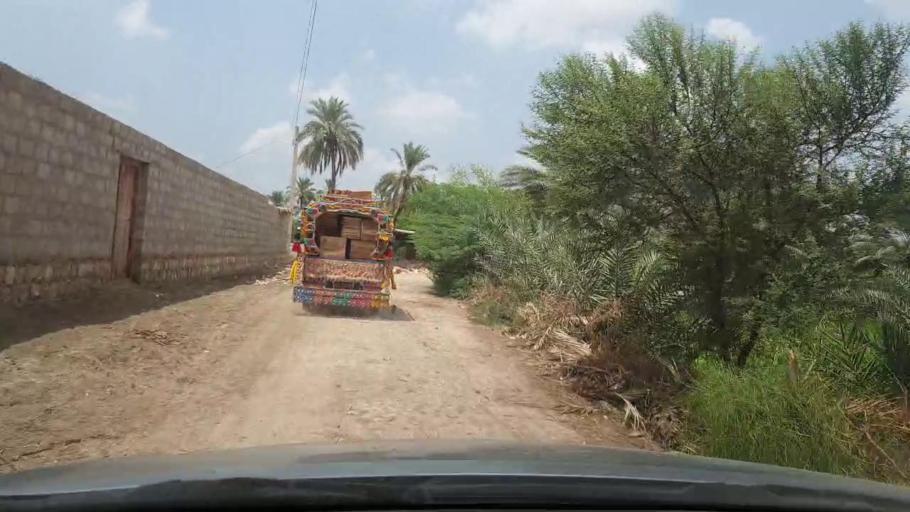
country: PK
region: Sindh
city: Kot Diji
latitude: 27.4196
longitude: 68.7635
